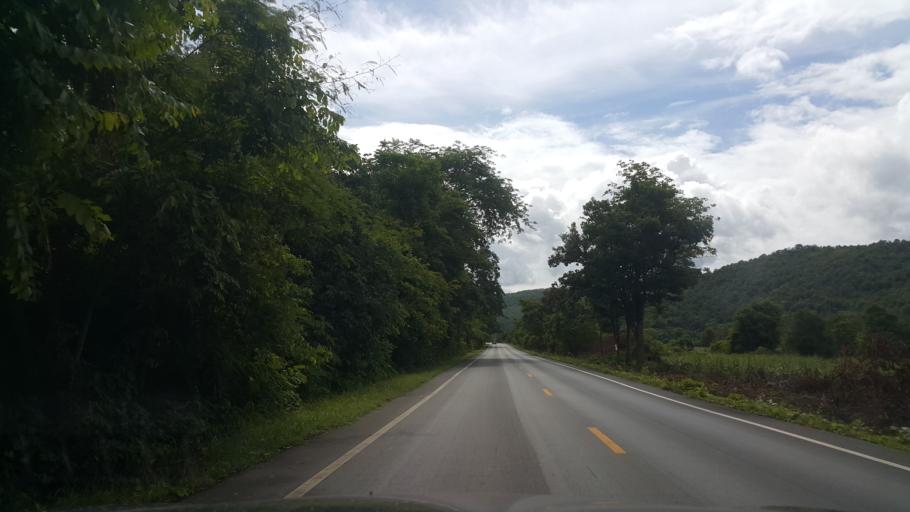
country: TH
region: Uttaradit
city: Thong Saen Khan
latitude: 17.3797
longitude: 100.2773
